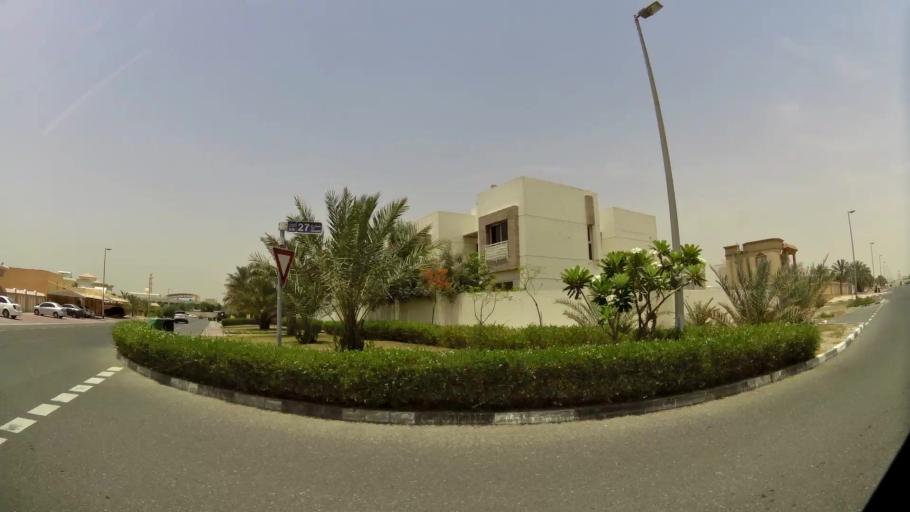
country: AE
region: Ash Shariqah
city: Sharjah
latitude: 25.1968
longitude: 55.3768
